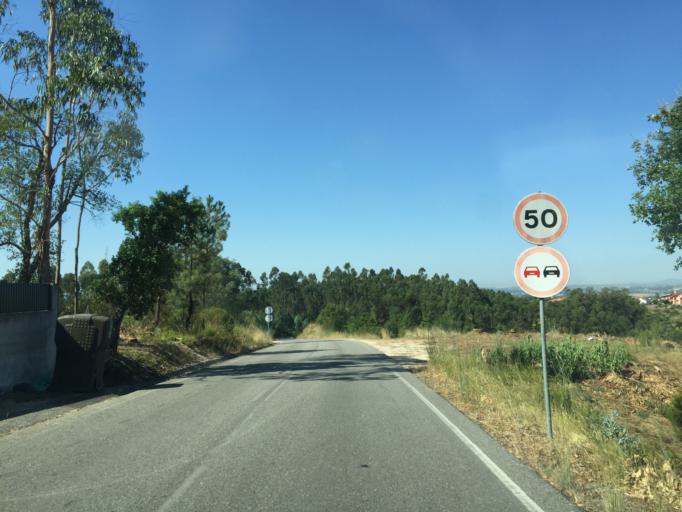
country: PT
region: Santarem
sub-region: Tomar
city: Tomar
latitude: 39.6066
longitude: -8.3422
